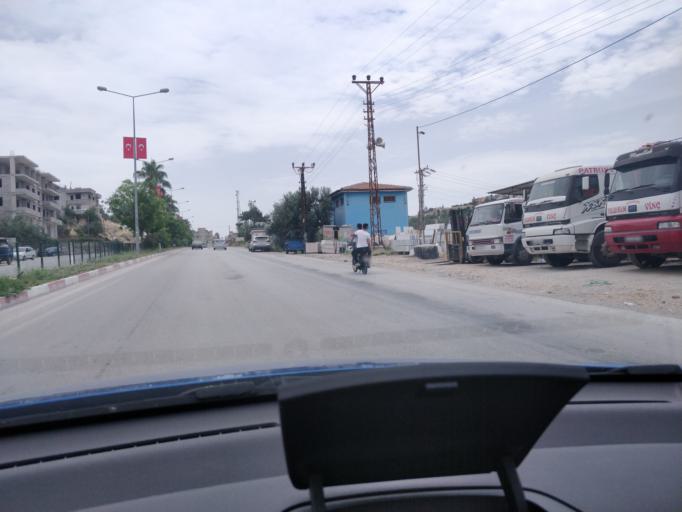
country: TR
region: Mersin
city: Mut
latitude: 36.6497
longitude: 33.4262
